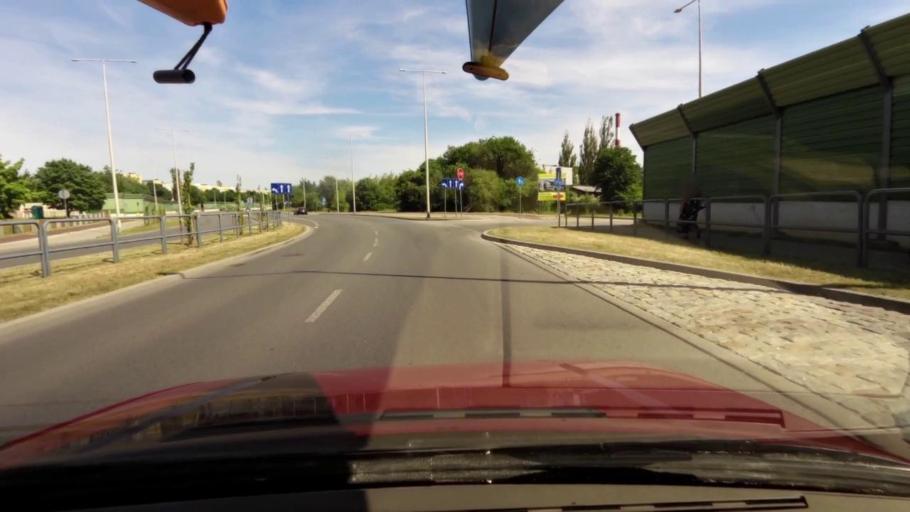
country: PL
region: Pomeranian Voivodeship
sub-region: Powiat slupski
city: Kobylnica
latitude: 54.4566
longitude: 16.9949
